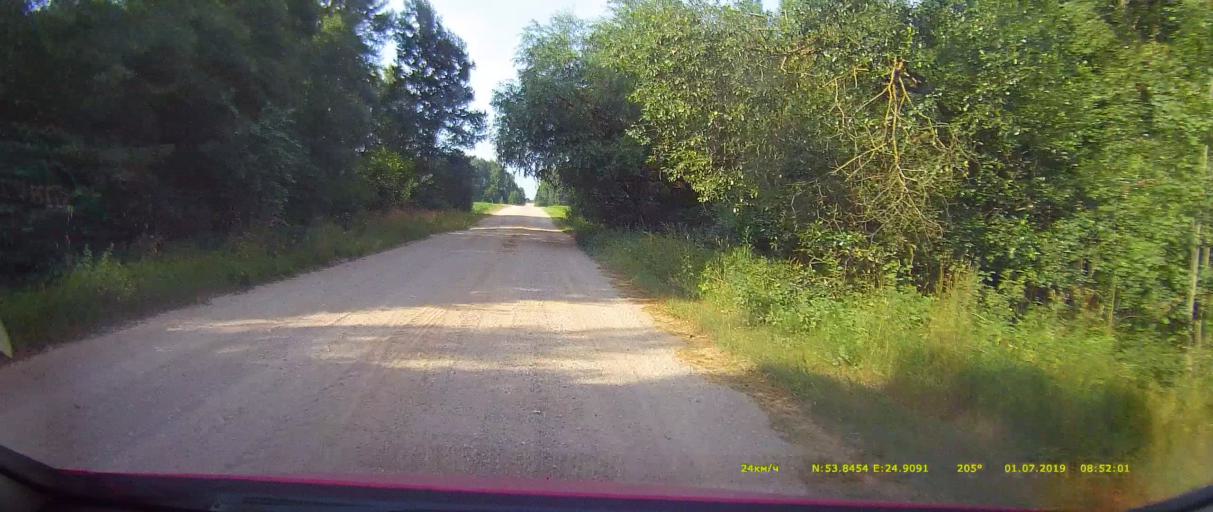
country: BY
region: Grodnenskaya
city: Shchuchin
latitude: 53.8456
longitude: 24.9093
